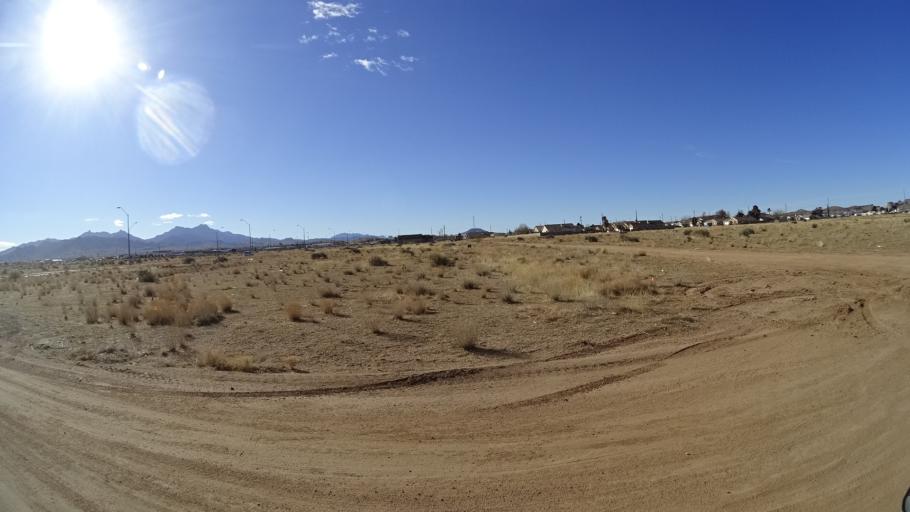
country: US
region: Arizona
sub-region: Mohave County
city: New Kingman-Butler
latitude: 35.2304
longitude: -114.0123
